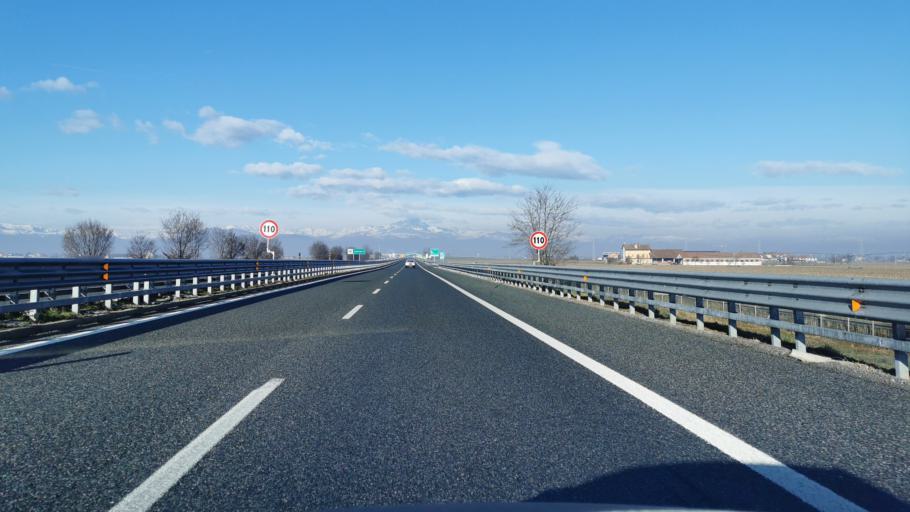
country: IT
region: Piedmont
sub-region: Provincia di Cuneo
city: Sant'Albano Stura
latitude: 44.4717
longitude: 7.7075
